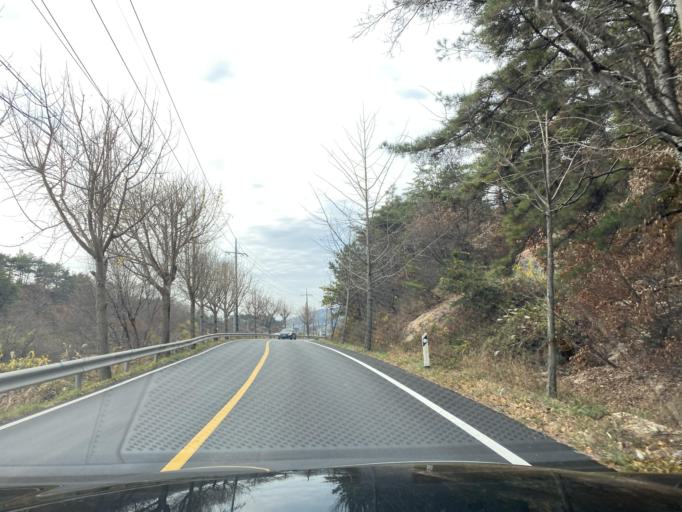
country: KR
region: Chungcheongnam-do
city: Hongsung
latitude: 36.6556
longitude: 126.6231
